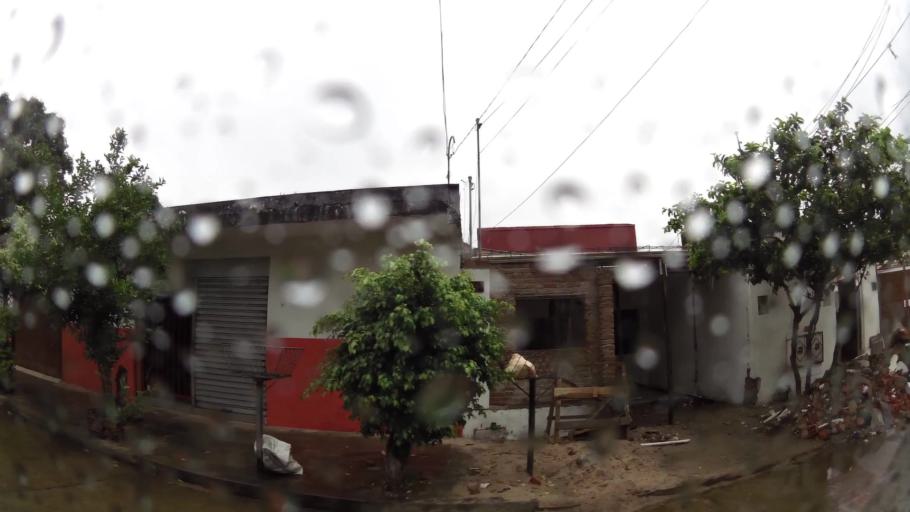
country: BO
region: Santa Cruz
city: Santa Cruz de la Sierra
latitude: -17.7720
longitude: -63.1491
